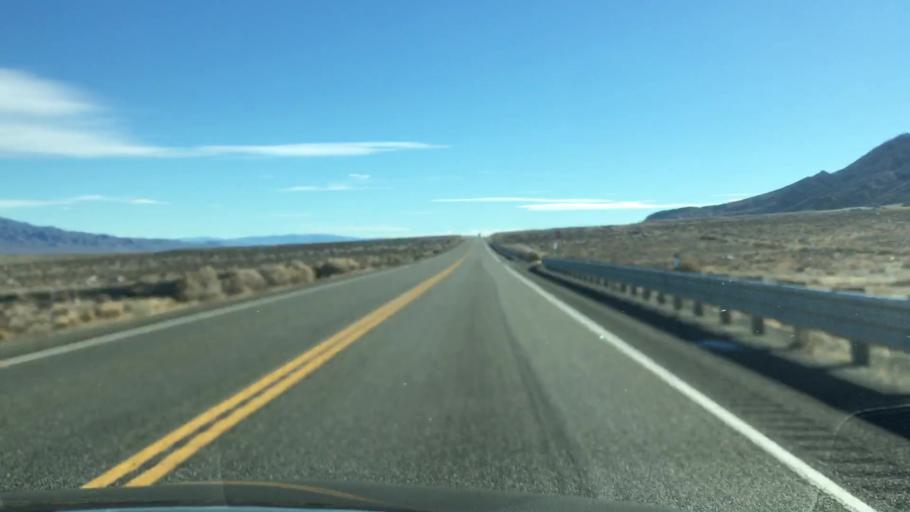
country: US
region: Nevada
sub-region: Mineral County
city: Hawthorne
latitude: 38.8113
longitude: -118.7649
